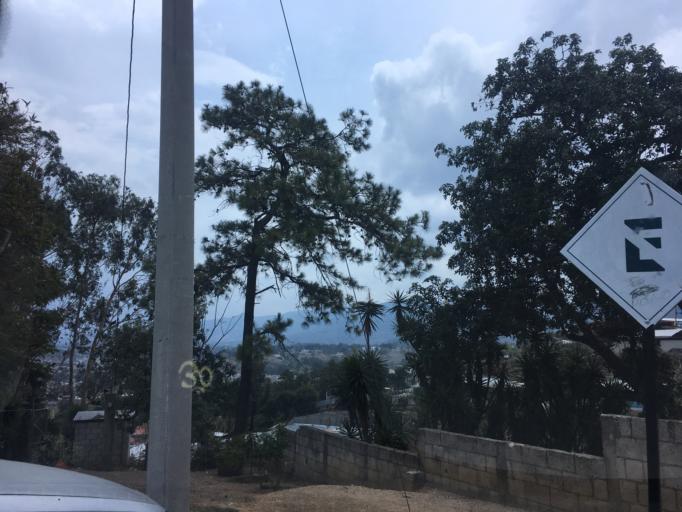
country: GT
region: Guatemala
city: Petapa
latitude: 14.5083
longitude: -90.5576
